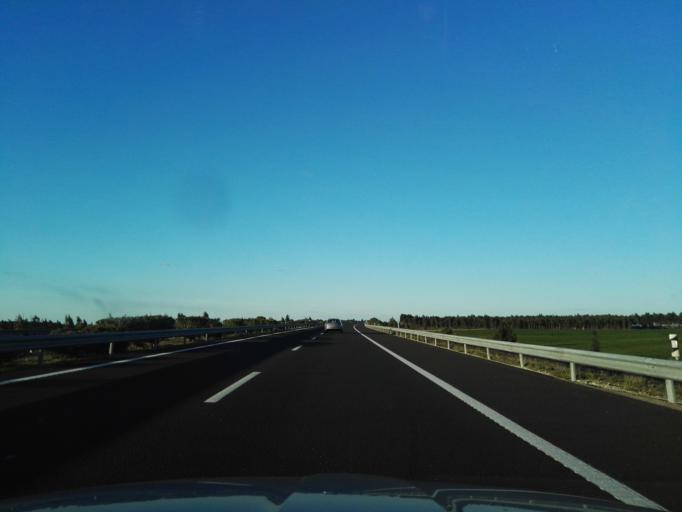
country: PT
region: Santarem
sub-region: Benavente
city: Poceirao
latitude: 38.7557
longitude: -8.6841
